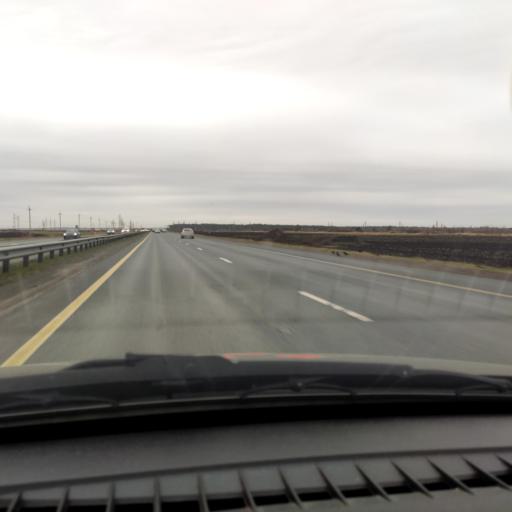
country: RU
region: Samara
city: Zhigulevsk
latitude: 53.5540
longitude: 49.5048
